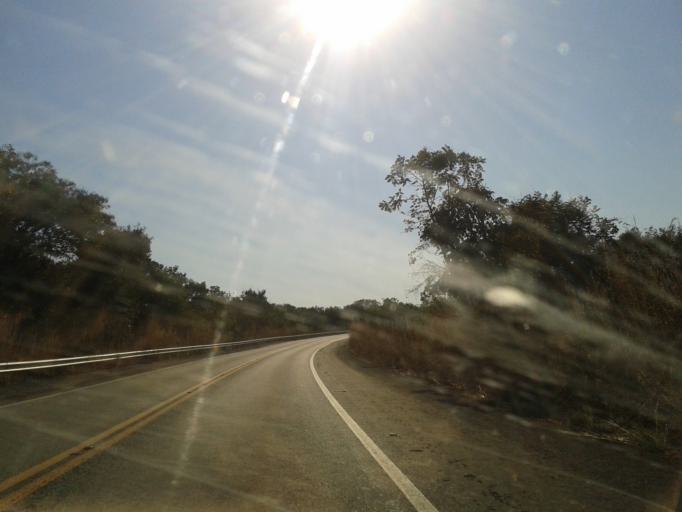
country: BR
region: Goias
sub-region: Mozarlandia
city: Mozarlandia
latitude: -14.9388
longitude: -50.5758
